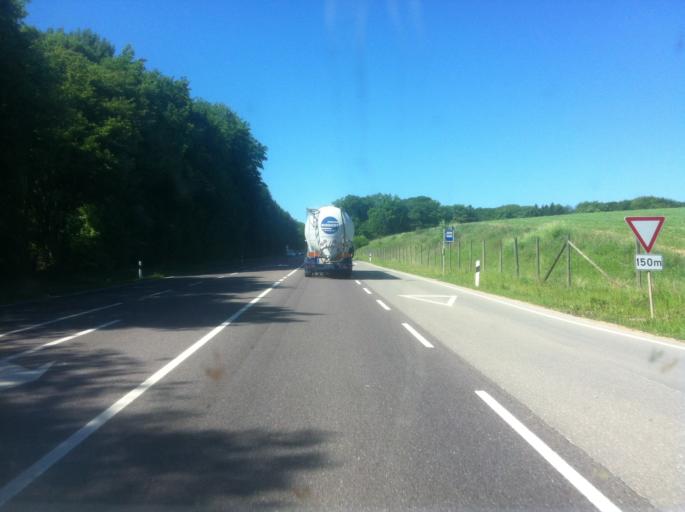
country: LU
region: Grevenmacher
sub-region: Canton d'Echternach
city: Bech
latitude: 49.7703
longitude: 6.3732
